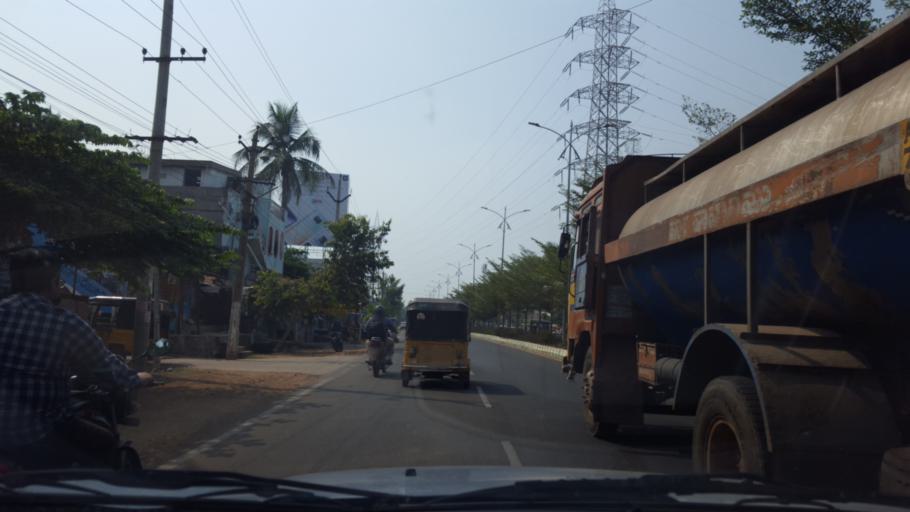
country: IN
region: Andhra Pradesh
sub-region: Vishakhapatnam
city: Vepagunta
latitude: 17.7591
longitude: 83.2216
